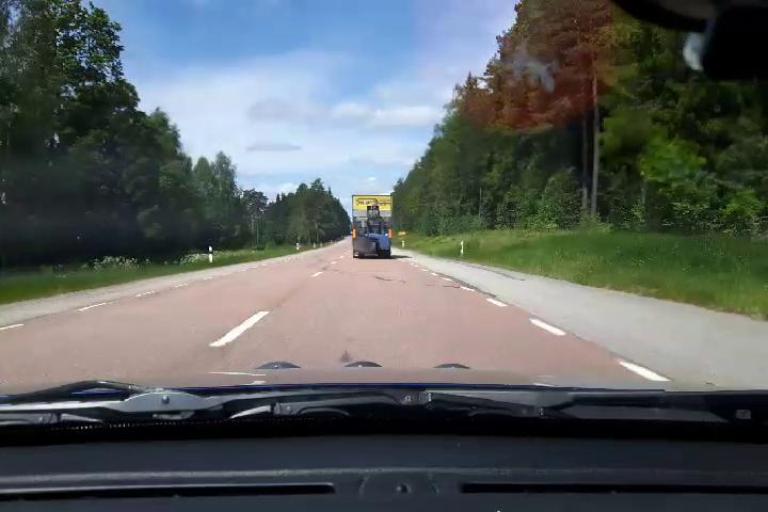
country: SE
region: Uppsala
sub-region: Osthammars Kommun
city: Bjorklinge
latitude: 60.1346
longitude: 17.5078
